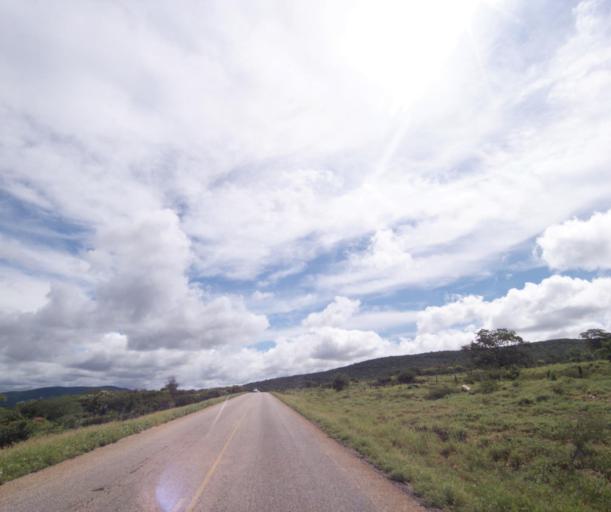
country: BR
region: Bahia
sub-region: Brumado
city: Brumado
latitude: -14.2092
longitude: -41.6279
